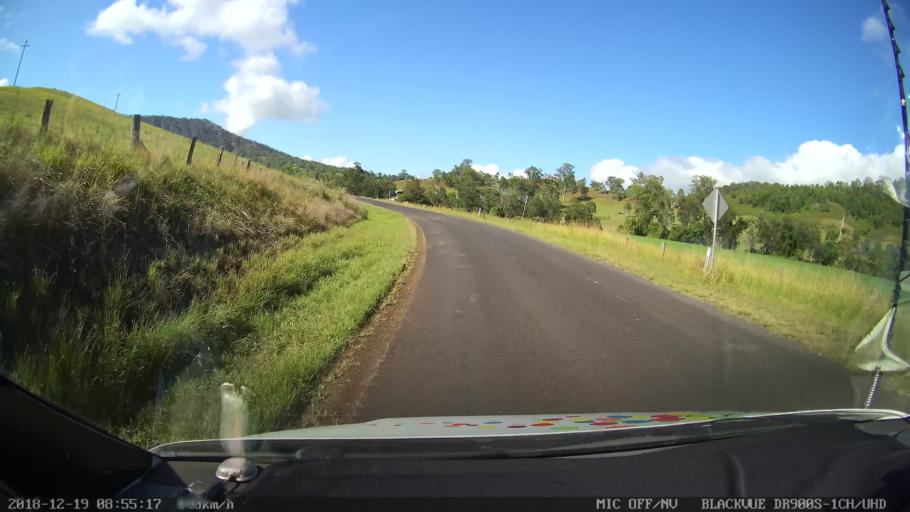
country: AU
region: New South Wales
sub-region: Kyogle
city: Kyogle
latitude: -28.4134
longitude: 152.9784
